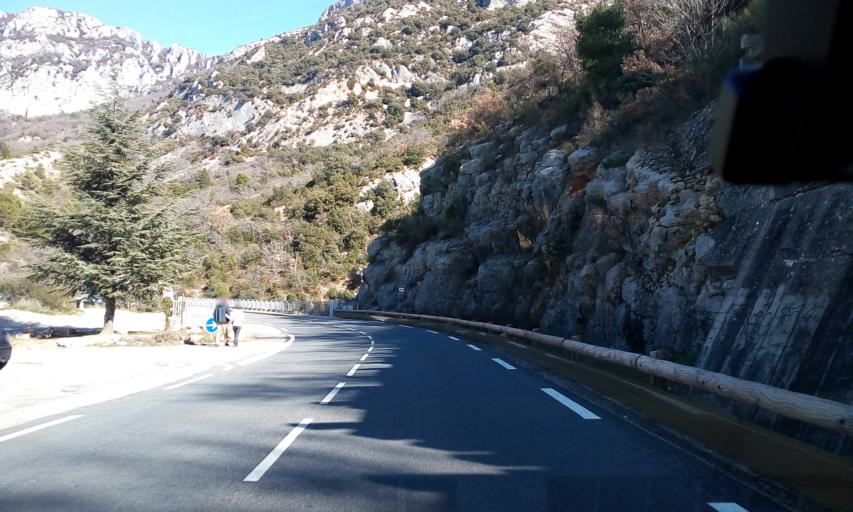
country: FR
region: Provence-Alpes-Cote d'Azur
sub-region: Departement des Alpes-de-Haute-Provence
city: Riez
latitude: 43.8009
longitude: 6.2486
